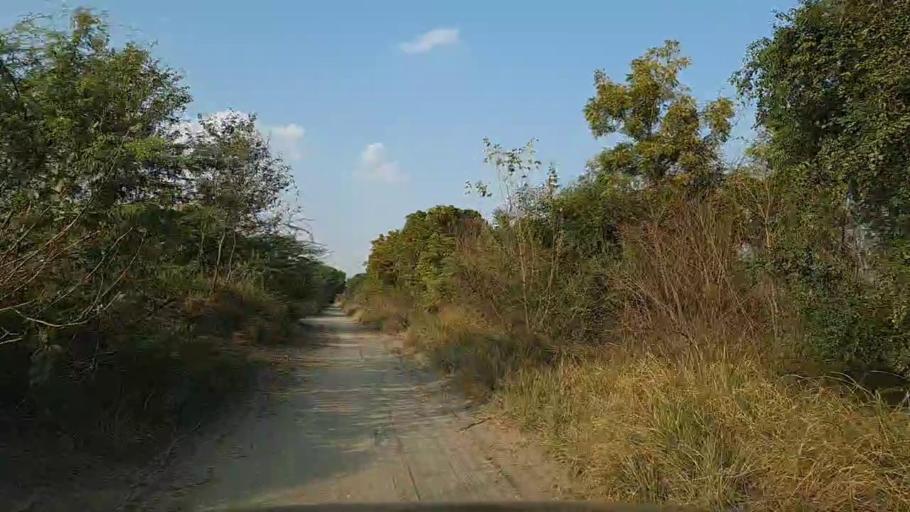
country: PK
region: Sindh
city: Jam Sahib
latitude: 26.3416
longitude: 68.5816
